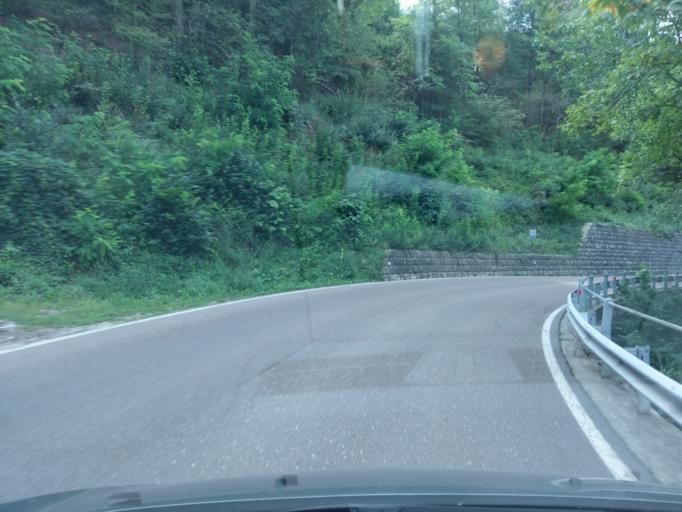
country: IT
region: Trentino-Alto Adige
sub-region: Provincia di Trento
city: Cagno
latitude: 46.3918
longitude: 11.0393
